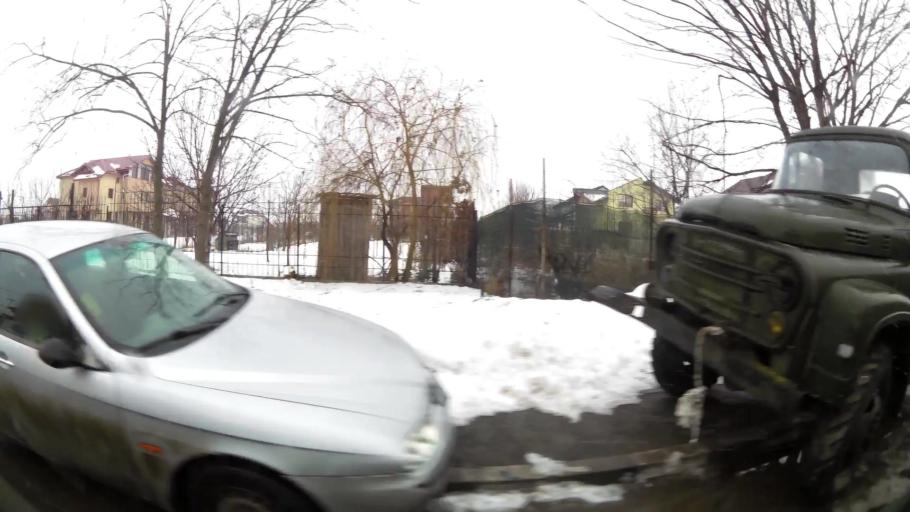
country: RO
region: Ilfov
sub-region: Comuna Mogosoaia
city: Mogosoaia
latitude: 44.5082
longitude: 26.0155
